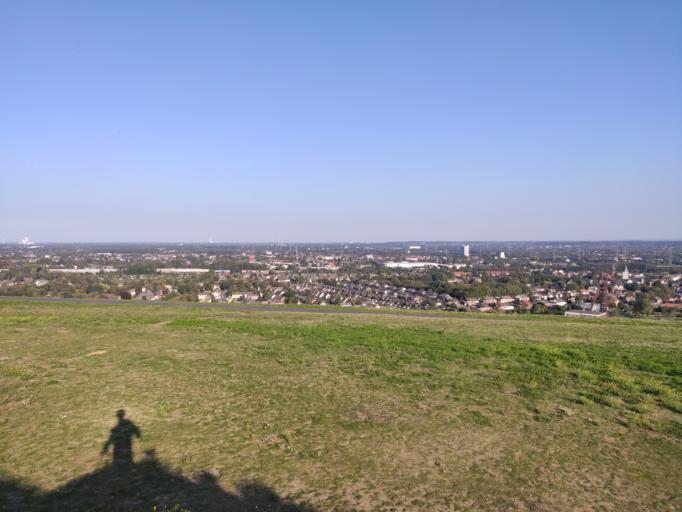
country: DE
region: North Rhine-Westphalia
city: Herten
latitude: 51.5674
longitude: 7.1705
